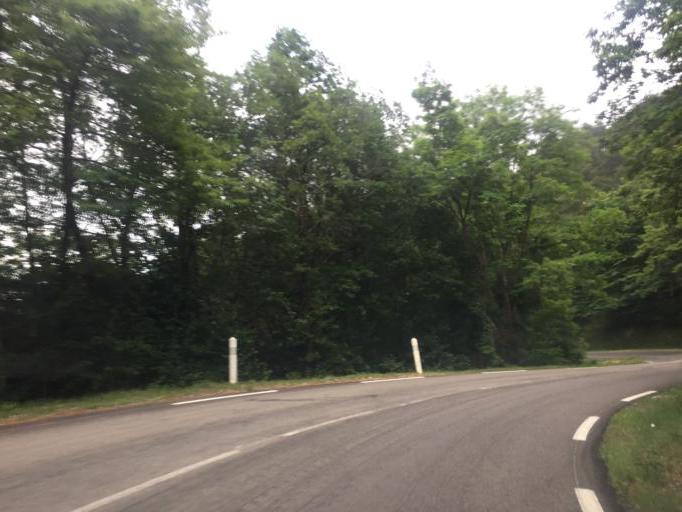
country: FR
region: Rhone-Alpes
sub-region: Departement de l'Ardeche
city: Privas
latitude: 44.7675
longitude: 4.5875
